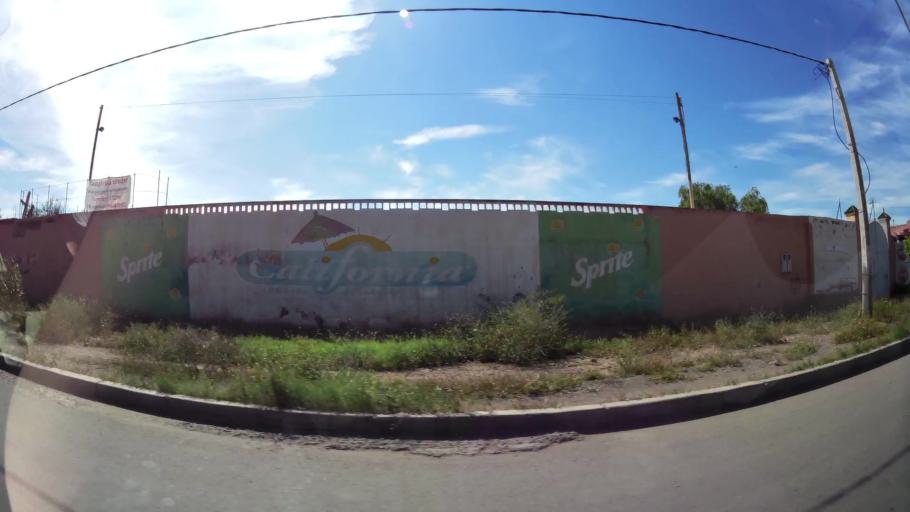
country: MA
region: Marrakech-Tensift-Al Haouz
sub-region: Marrakech
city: Marrakesh
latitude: 31.6528
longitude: -8.0603
